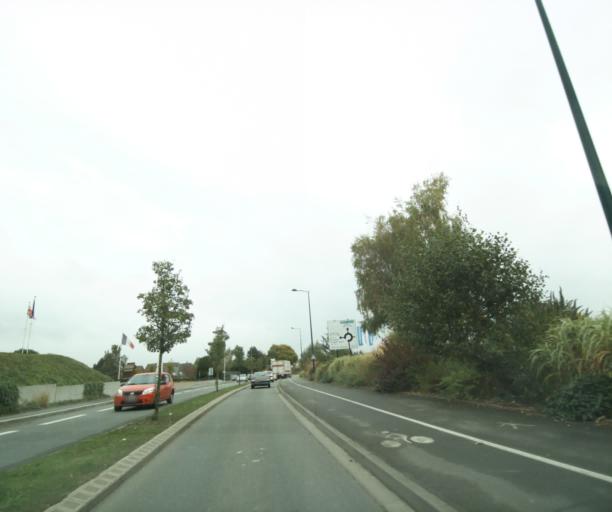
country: FR
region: Nord-Pas-de-Calais
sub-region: Departement du Nord
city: Bondues
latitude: 50.6925
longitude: 3.0881
